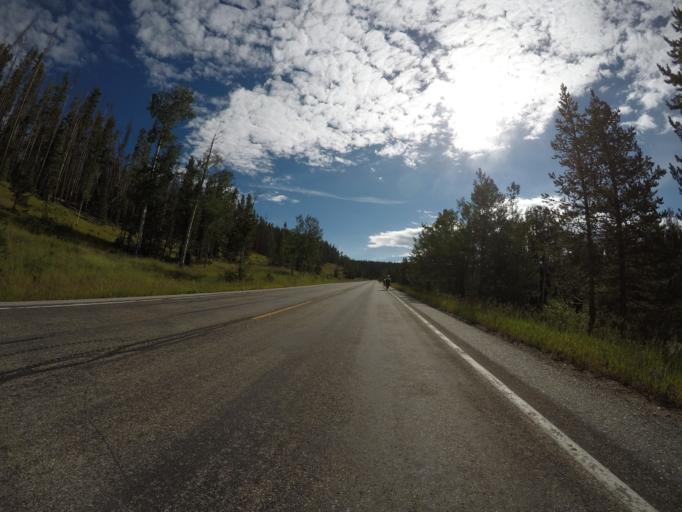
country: US
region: Wyoming
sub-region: Carbon County
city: Saratoga
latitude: 41.3280
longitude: -106.4852
